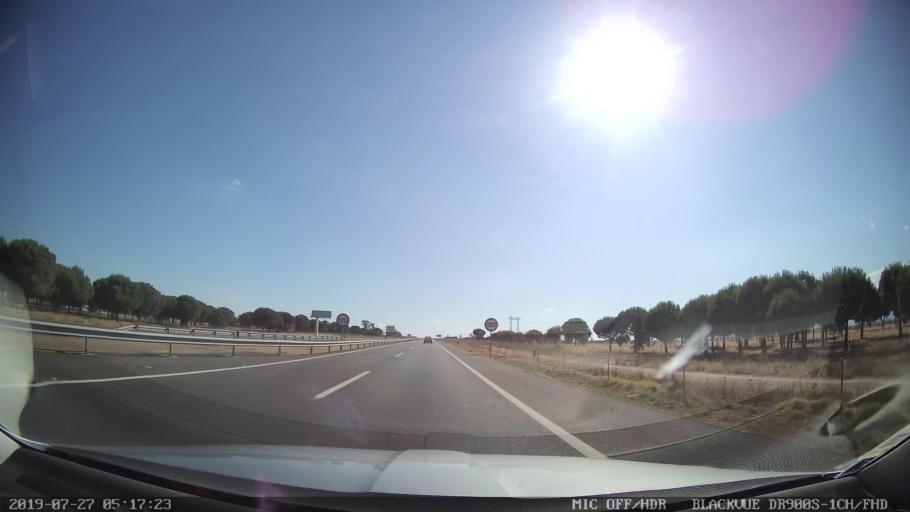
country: ES
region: Castille-La Mancha
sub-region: Province of Toledo
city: Maqueda
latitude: 40.0476
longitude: -4.3910
